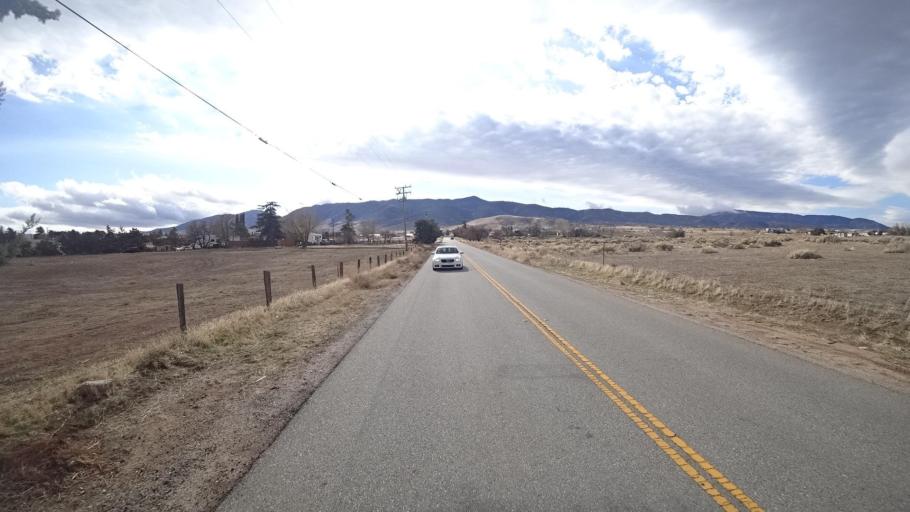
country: US
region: California
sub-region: Kern County
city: Golden Hills
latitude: 35.1275
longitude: -118.4773
